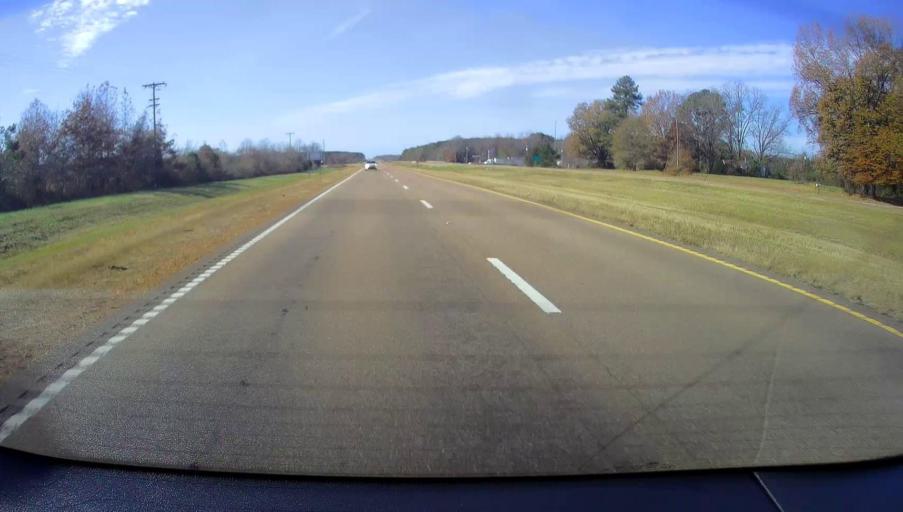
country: US
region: Mississippi
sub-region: Benton County
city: Ashland
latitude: 34.9461
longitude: -89.2068
